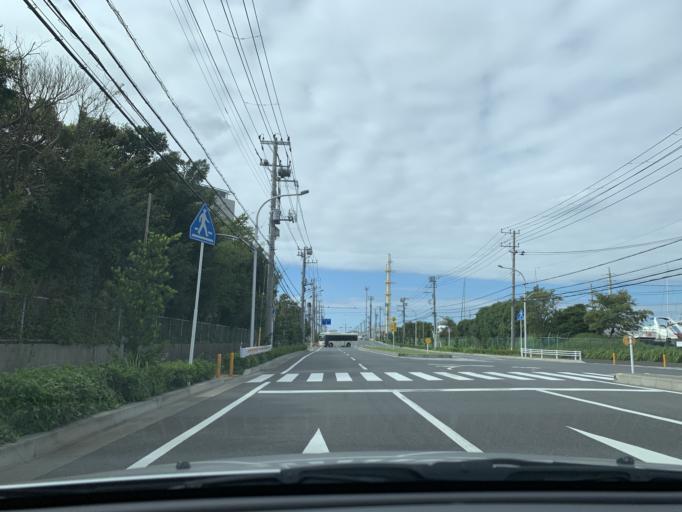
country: JP
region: Tokyo
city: Urayasu
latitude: 35.6269
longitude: 139.8975
